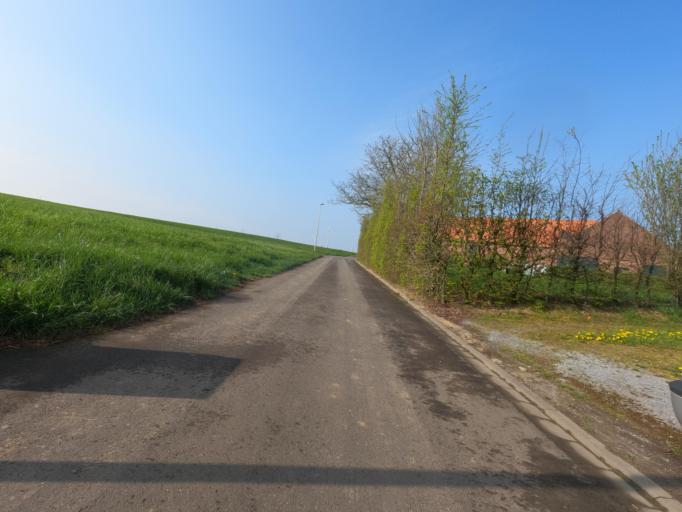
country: DE
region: North Rhine-Westphalia
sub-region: Regierungsbezirk Koln
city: Heinsberg
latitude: 51.0349
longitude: 6.1275
